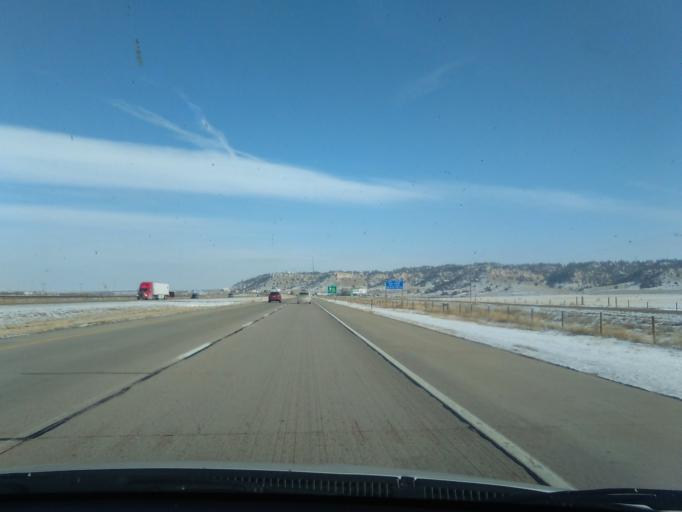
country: US
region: Wyoming
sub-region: Laramie County
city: Pine Bluffs
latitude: 41.1616
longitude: -104.0966
